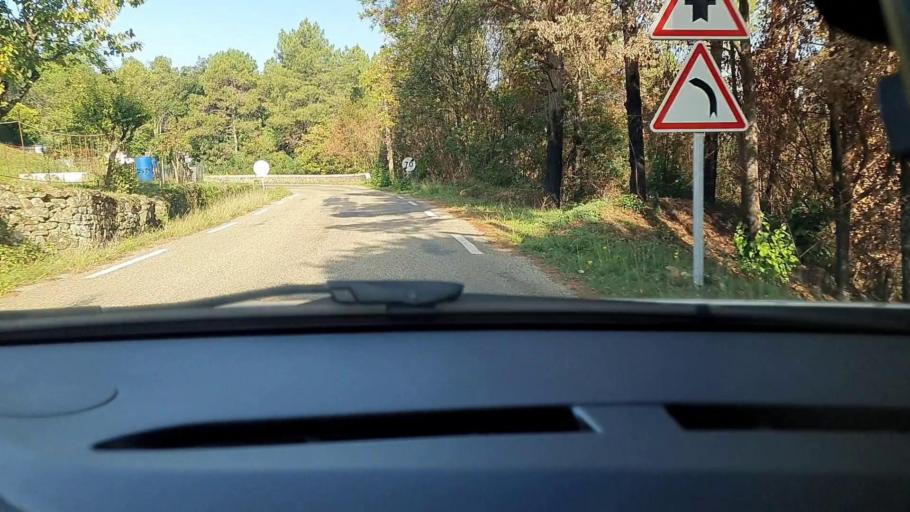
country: FR
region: Languedoc-Roussillon
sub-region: Departement du Gard
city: Besseges
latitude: 44.3149
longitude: 4.0866
